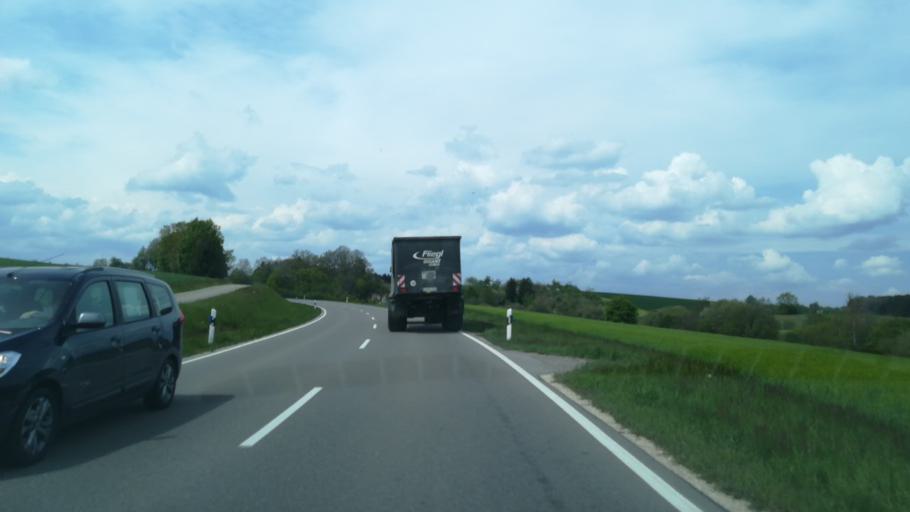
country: DE
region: Baden-Wuerttemberg
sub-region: Tuebingen Region
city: Messkirch
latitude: 48.0095
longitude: 9.1149
